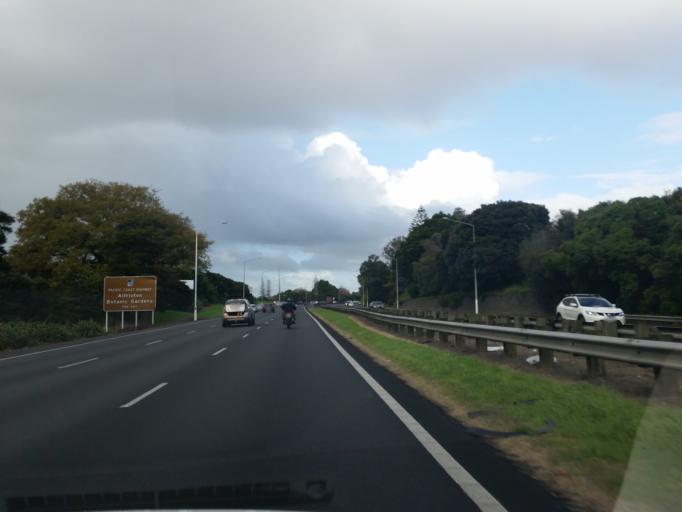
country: NZ
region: Auckland
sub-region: Auckland
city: Manukau City
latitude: -37.0080
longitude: 174.9004
